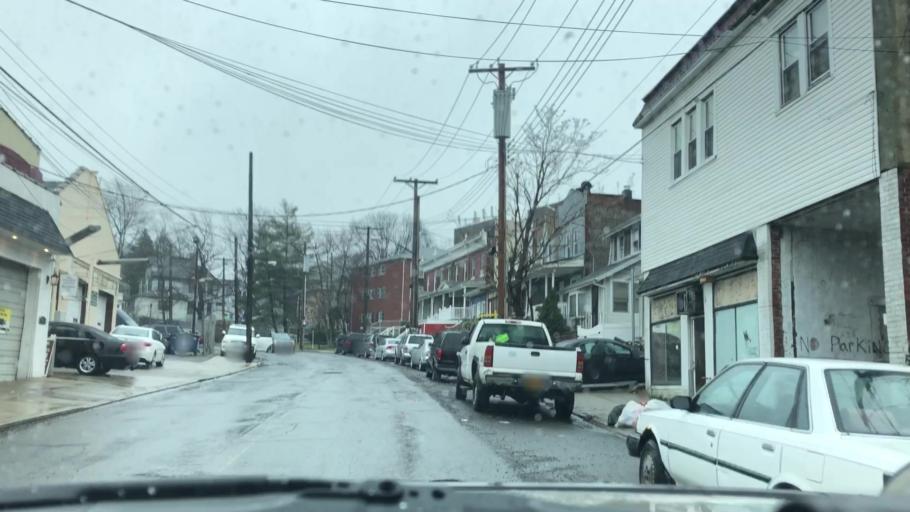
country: US
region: New Jersey
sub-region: Hudson County
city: Bayonne
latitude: 40.6336
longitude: -74.0967
